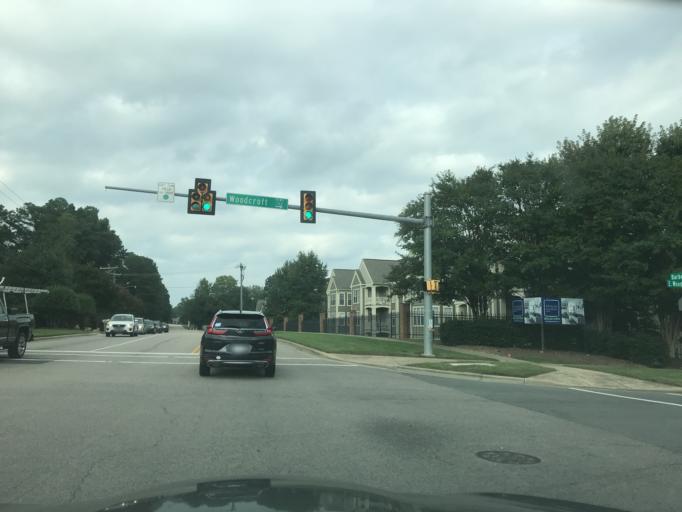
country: US
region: North Carolina
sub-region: Durham County
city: Durham
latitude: 35.9172
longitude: -78.9160
